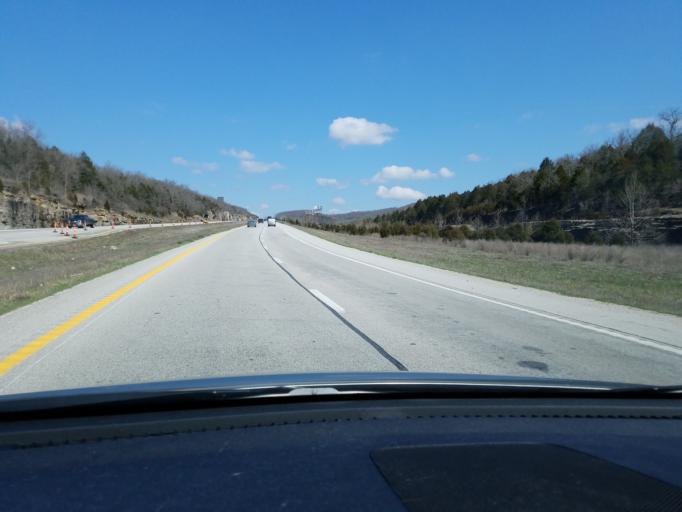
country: US
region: Missouri
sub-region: Taney County
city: Merriam Woods
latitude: 36.7705
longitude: -93.2241
